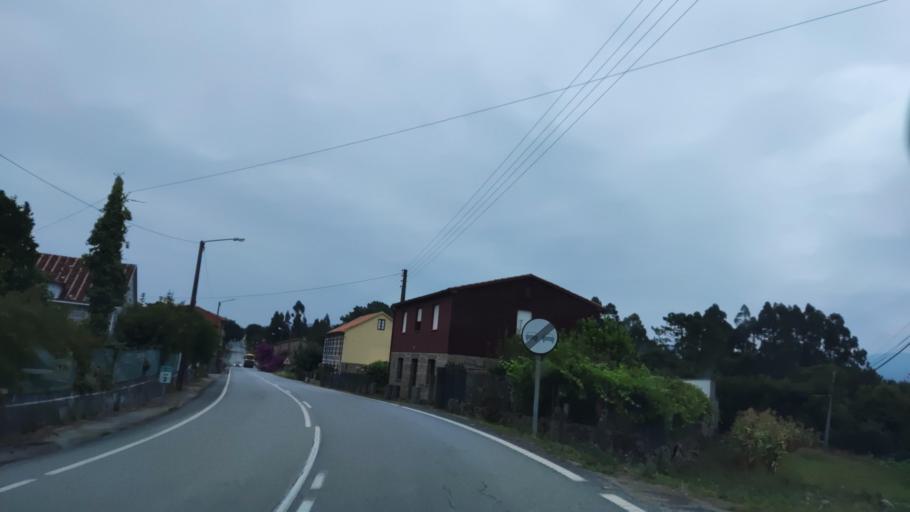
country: ES
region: Galicia
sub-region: Provincia da Coruna
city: Padron
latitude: 42.7144
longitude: -8.6943
